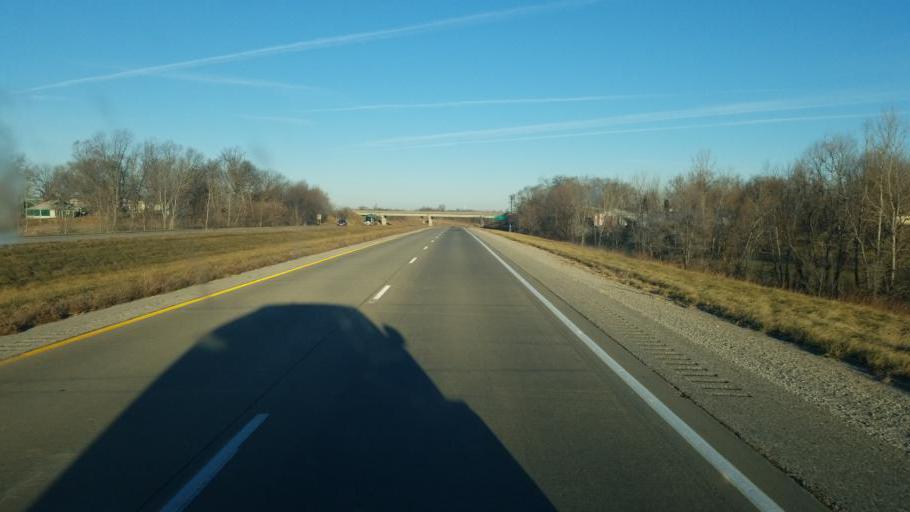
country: US
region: Iowa
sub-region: Mahaska County
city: Oskaloosa
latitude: 41.2827
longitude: -92.6701
